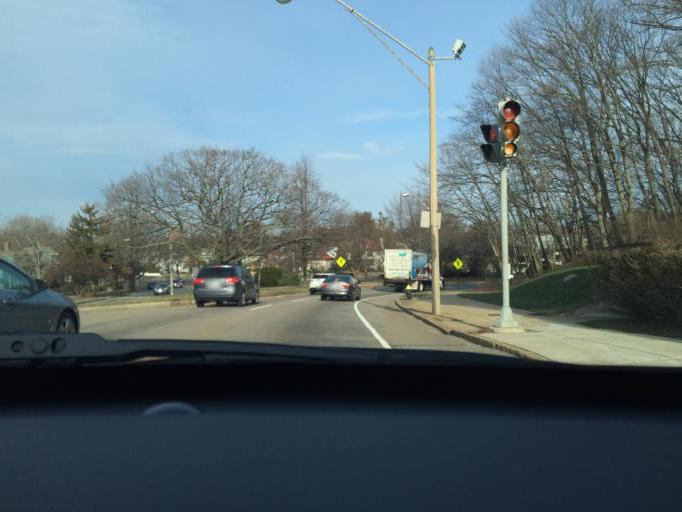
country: US
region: Massachusetts
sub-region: Suffolk County
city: Jamaica Plain
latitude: 42.3082
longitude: -71.1227
